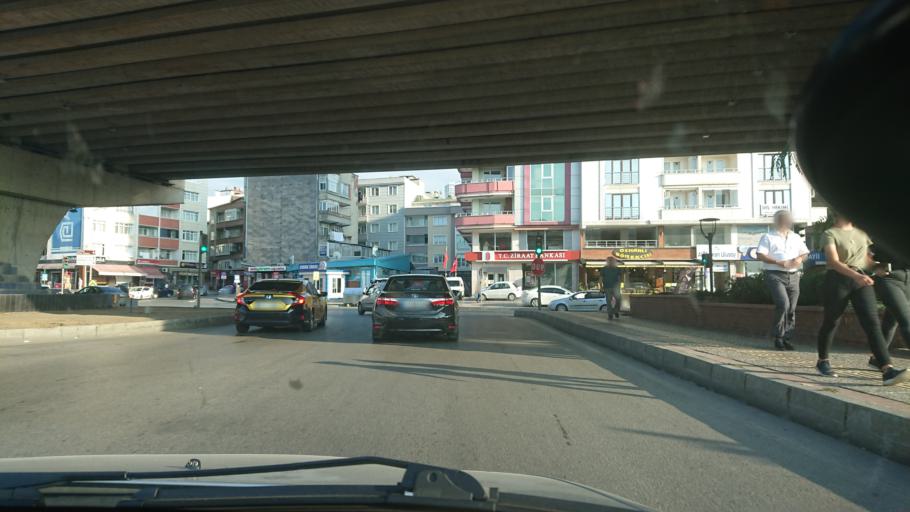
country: TR
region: Samsun
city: Samsun
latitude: 41.2724
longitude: 36.3657
